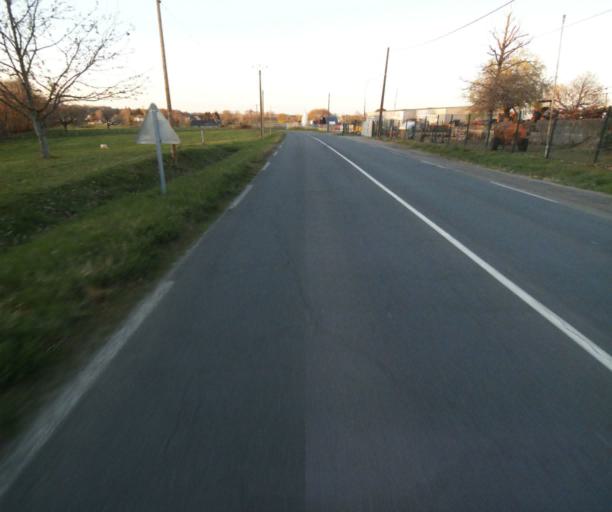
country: FR
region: Limousin
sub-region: Departement de la Correze
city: Sainte-Fereole
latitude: 45.2857
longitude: 1.5679
